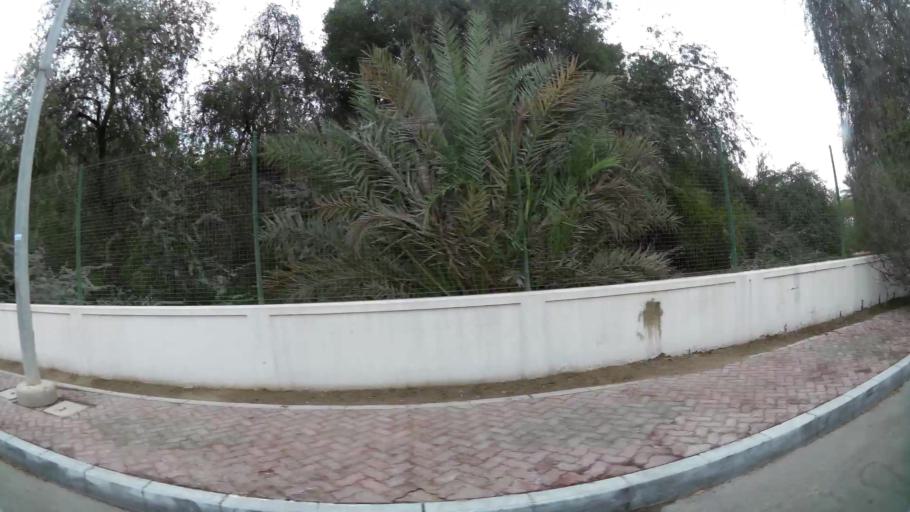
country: AE
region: Abu Dhabi
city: Abu Dhabi
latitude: 24.4288
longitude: 54.3772
